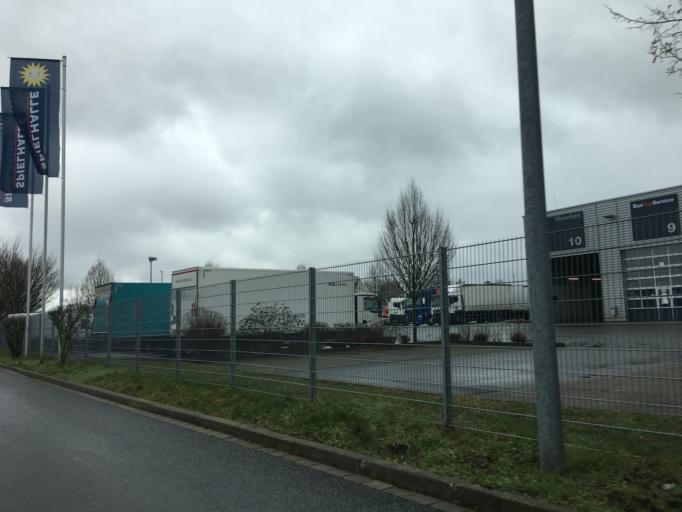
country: DE
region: North Rhine-Westphalia
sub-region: Regierungsbezirk Munster
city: Senden
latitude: 51.9029
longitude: 7.4886
